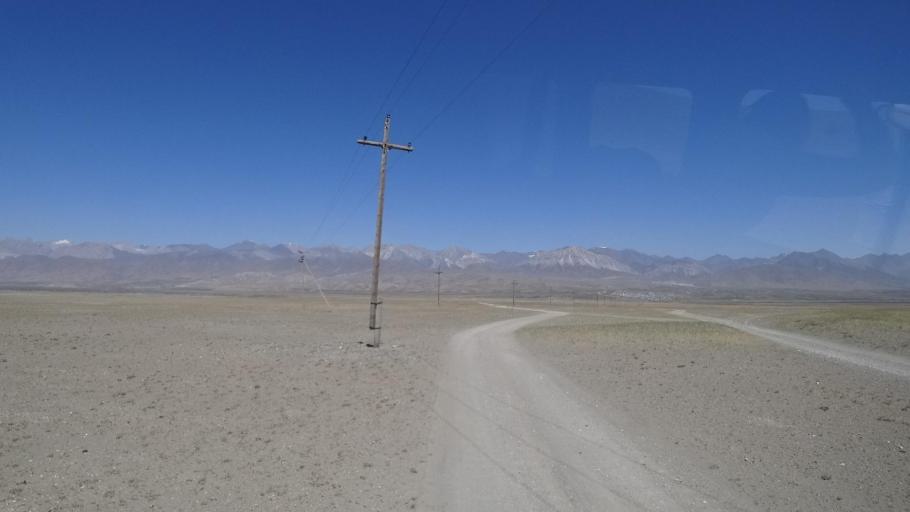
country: KG
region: Osh
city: Gul'cha
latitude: 39.6096
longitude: 72.8752
